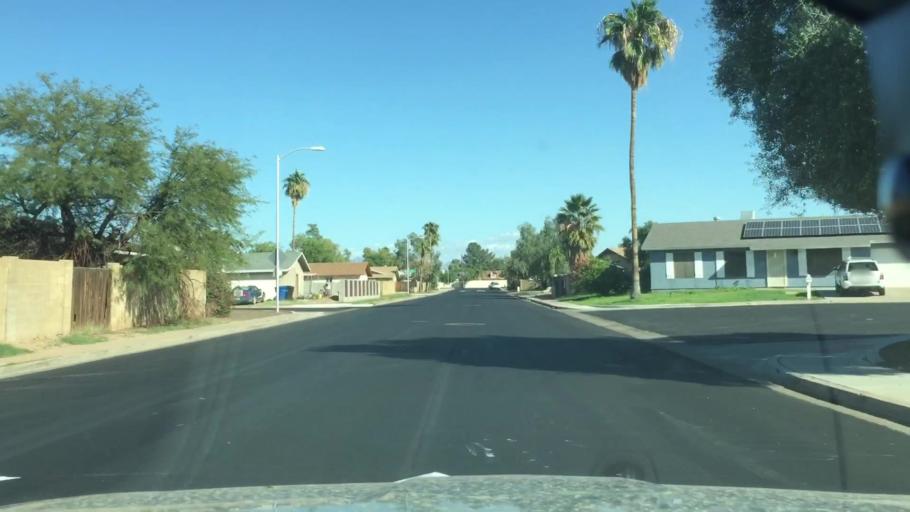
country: US
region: Arizona
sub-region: Maricopa County
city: Gilbert
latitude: 33.4046
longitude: -111.7569
